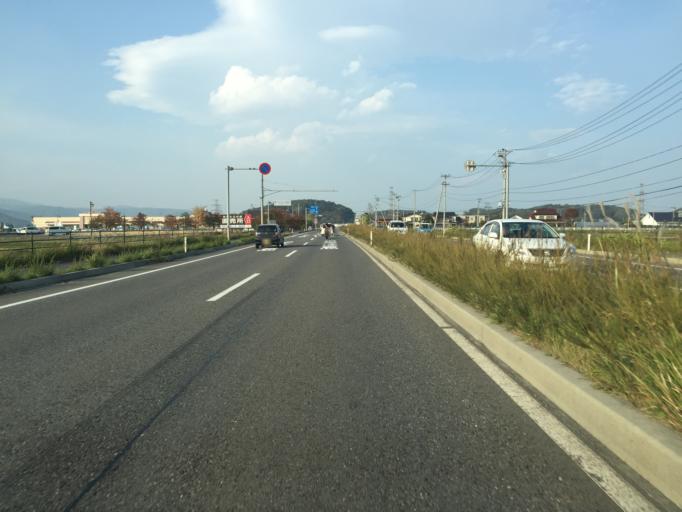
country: JP
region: Fukushima
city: Motomiya
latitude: 37.5370
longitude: 140.3969
